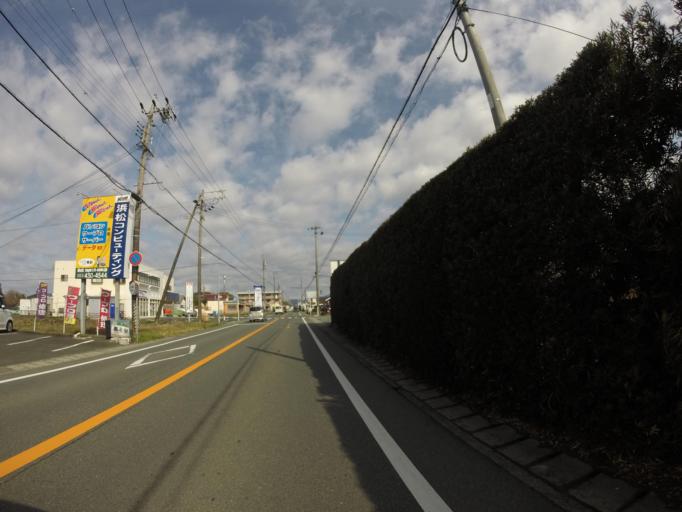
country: JP
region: Shizuoka
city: Hamakita
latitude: 34.7957
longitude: 137.7008
